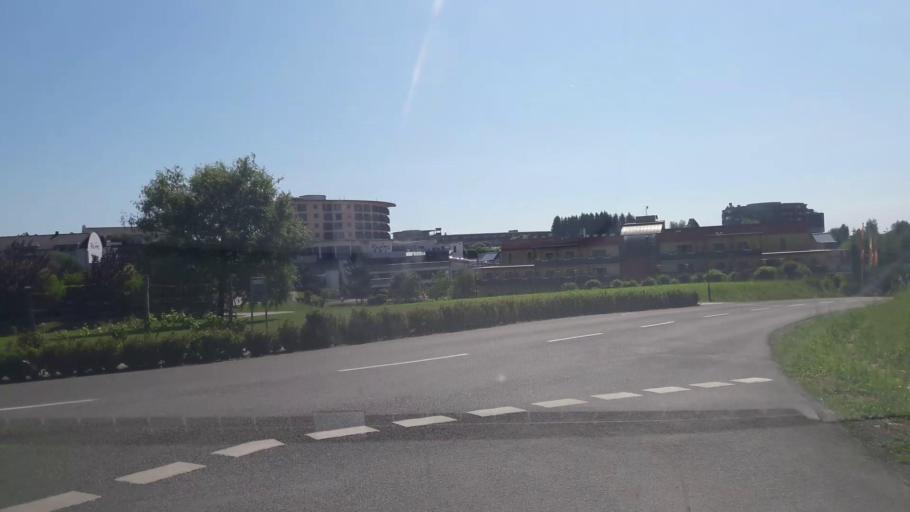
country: AT
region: Burgenland
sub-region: Politischer Bezirk Gussing
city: Stegersbach
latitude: 47.1720
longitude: 16.1465
